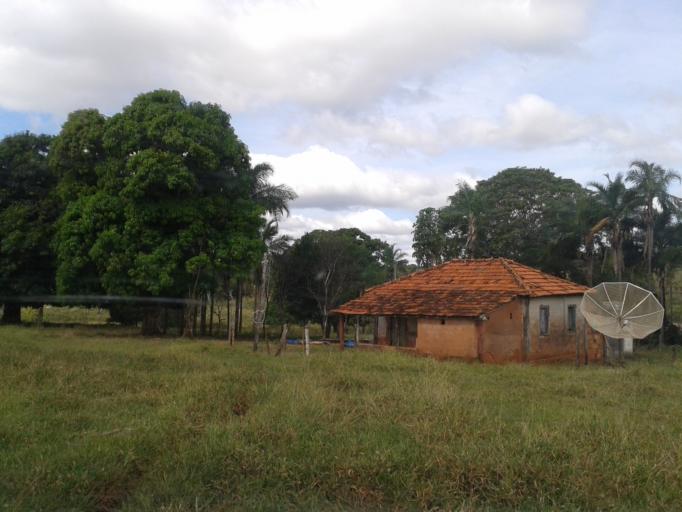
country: BR
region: Minas Gerais
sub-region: Campina Verde
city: Campina Verde
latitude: -19.4294
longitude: -49.7028
